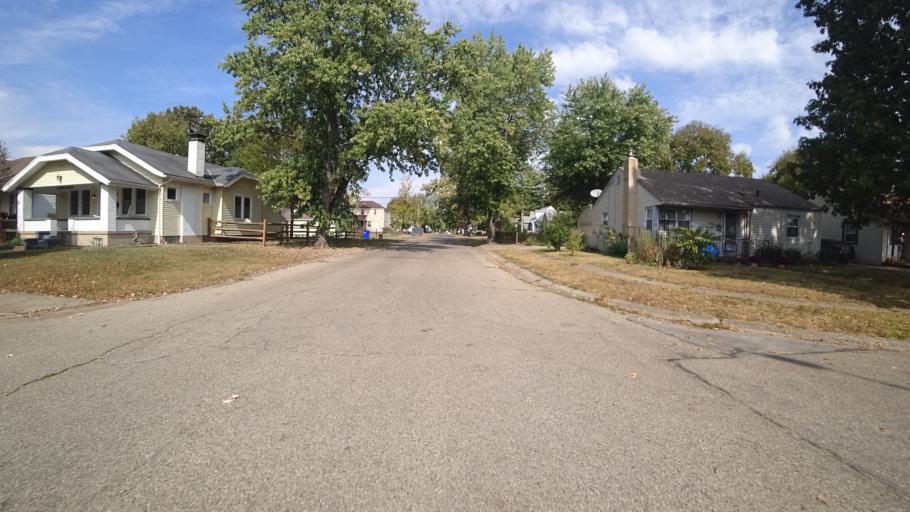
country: US
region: Ohio
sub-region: Butler County
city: Fairfield
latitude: 39.3627
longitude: -84.5514
